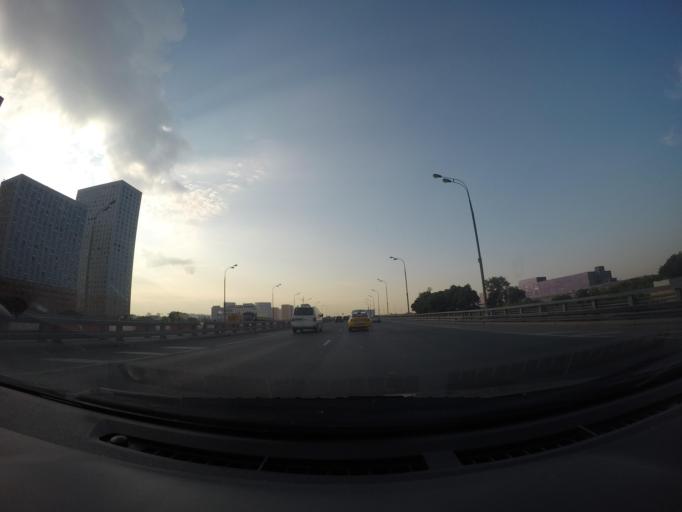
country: RU
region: Moscow
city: Lefortovo
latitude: 55.7280
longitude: 37.7086
